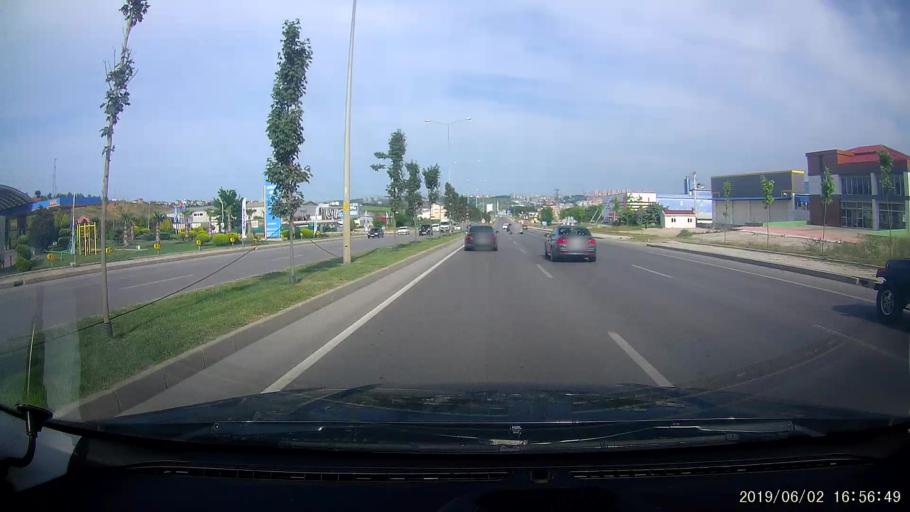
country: TR
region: Samsun
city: Samsun
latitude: 41.2920
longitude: 36.2657
